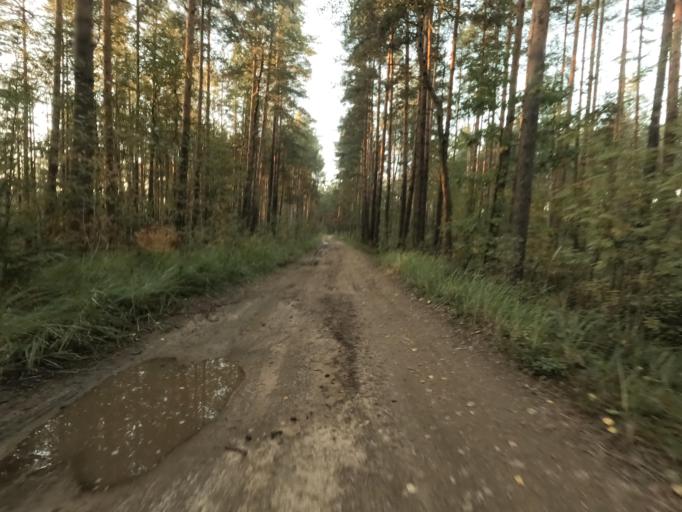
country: RU
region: Leningrad
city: Otradnoye
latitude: 59.8416
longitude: 30.8030
